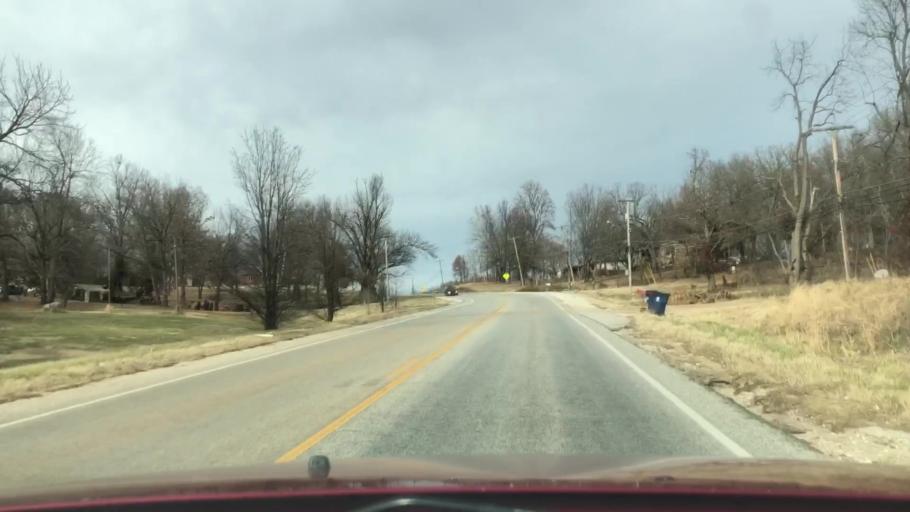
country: US
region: Missouri
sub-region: Greene County
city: Springfield
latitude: 37.2776
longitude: -93.2631
